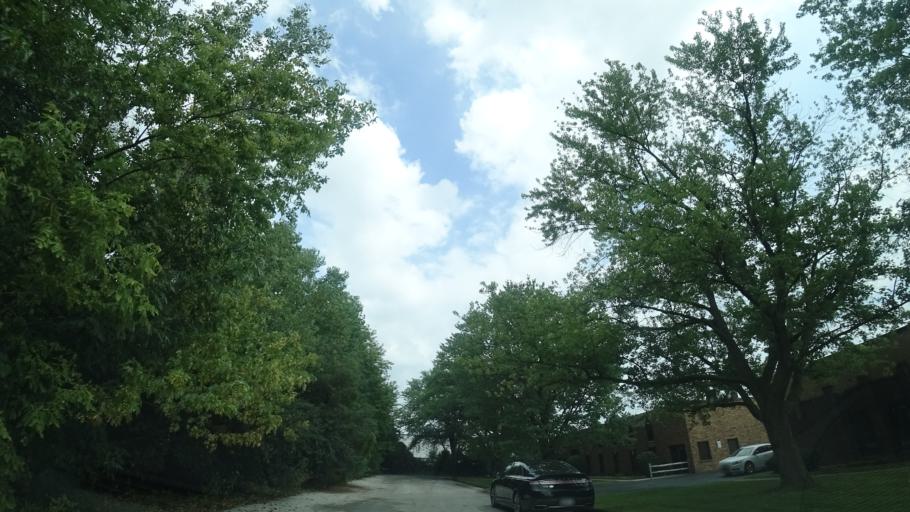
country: US
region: Illinois
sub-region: Cook County
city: Crestwood
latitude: 41.6814
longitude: -87.7647
